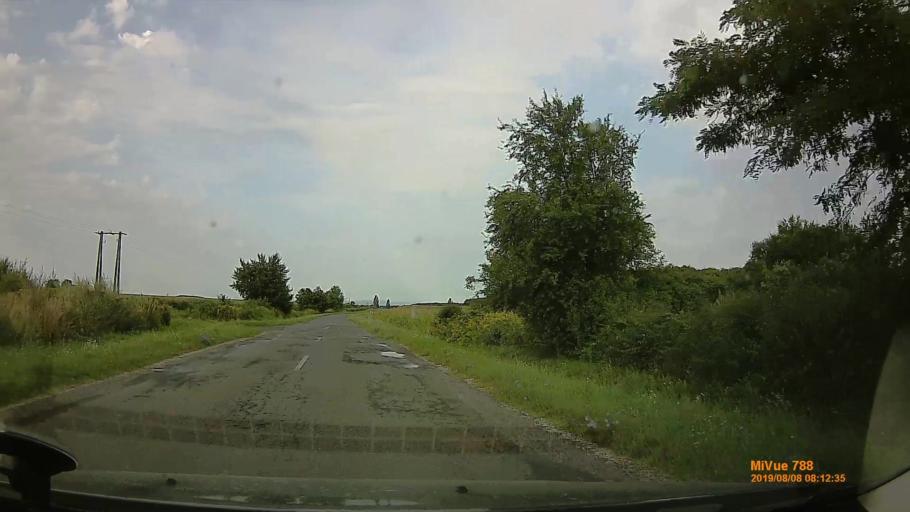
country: HU
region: Zala
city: Murakeresztur
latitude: 46.4128
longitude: 16.8700
